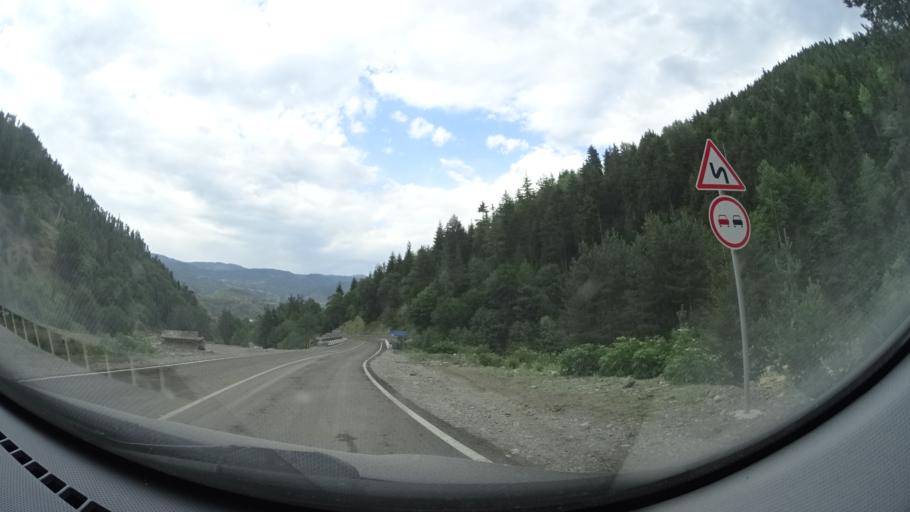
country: GE
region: Samtskhe-Javakheti
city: Adigeni
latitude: 41.6728
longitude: 42.6410
